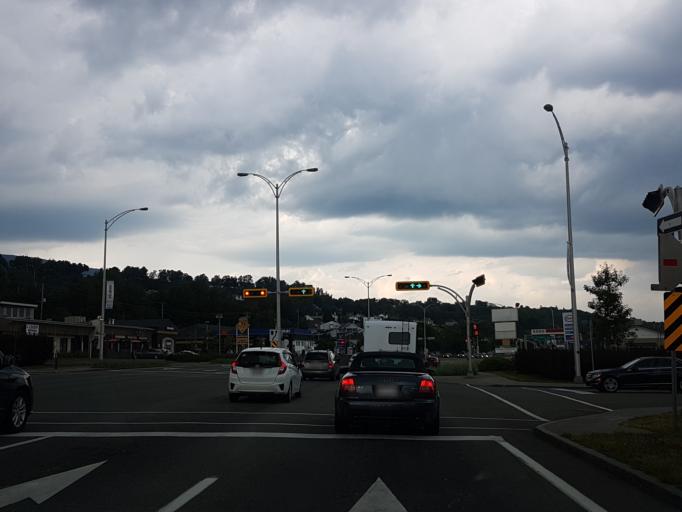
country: CA
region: Quebec
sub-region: Capitale-Nationale
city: Beaupre
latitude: 47.0412
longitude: -70.8971
